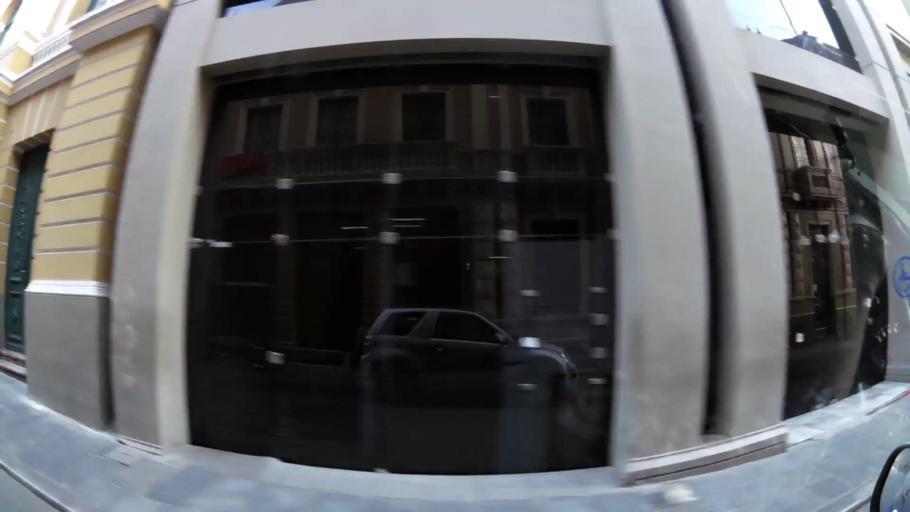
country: BO
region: La Paz
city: La Paz
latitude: -16.4964
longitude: -68.1330
